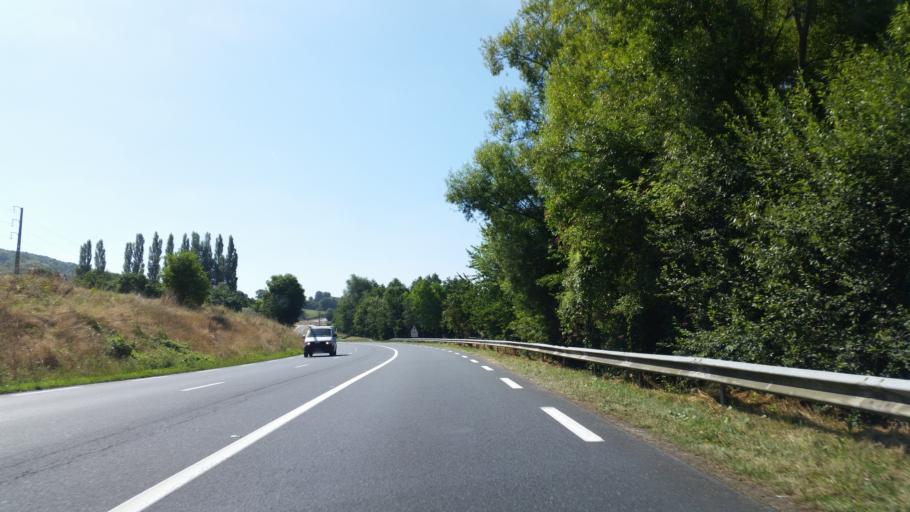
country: FR
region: Lower Normandy
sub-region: Departement du Calvados
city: Saint-Gatien-des-Bois
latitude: 49.2566
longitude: 0.2184
